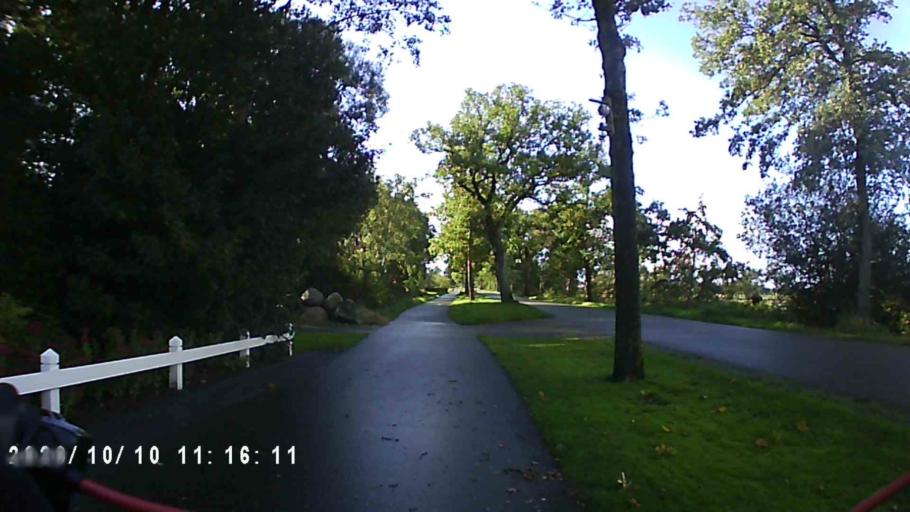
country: NL
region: Friesland
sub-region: Gemeente Smallingerland
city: Drachtstercompagnie
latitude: 53.1004
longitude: 6.2002
